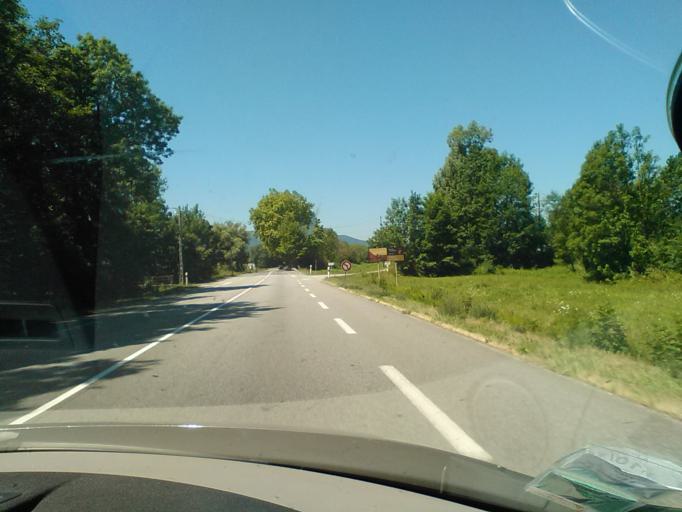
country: FR
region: Rhone-Alpes
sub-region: Departement de la Savoie
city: Les Marches
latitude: 45.5071
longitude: 6.0247
